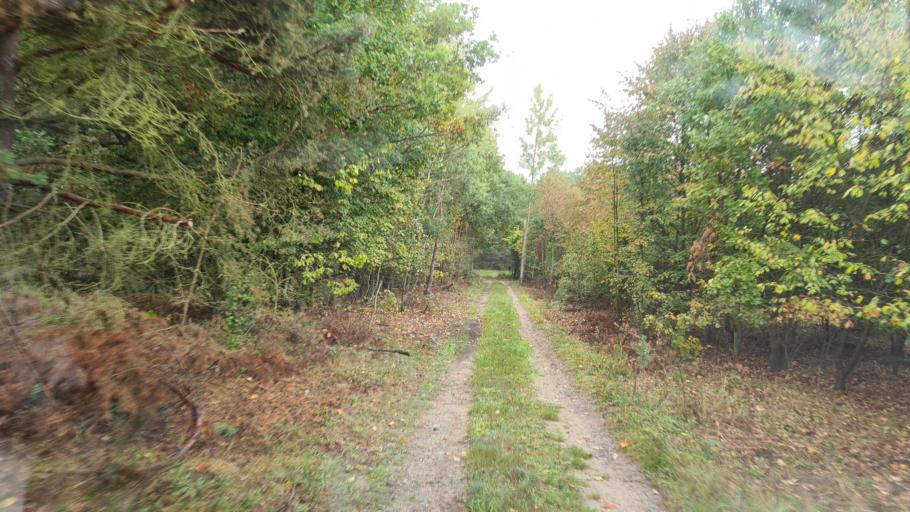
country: DE
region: Brandenburg
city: Altdobern
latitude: 51.6723
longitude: 14.1081
